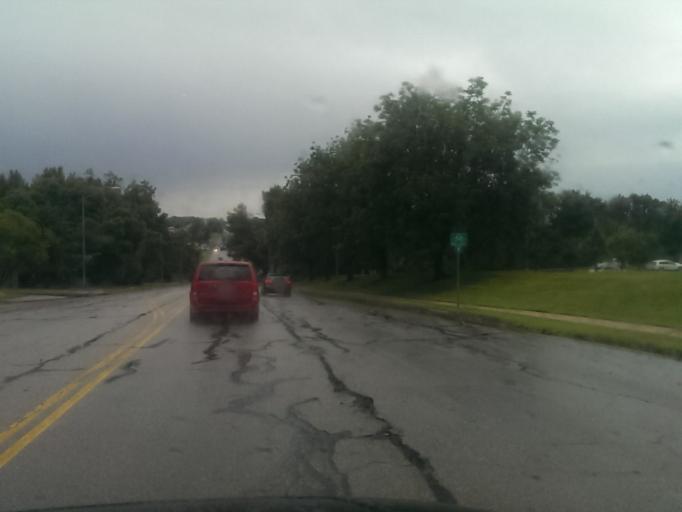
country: US
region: Kansas
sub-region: Johnson County
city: Leawood
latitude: 38.9435
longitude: -94.5826
